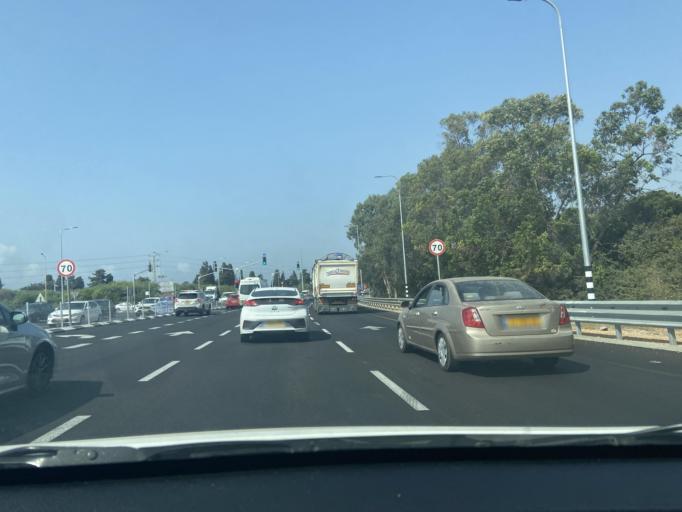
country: IL
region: Northern District
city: `Akko
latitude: 32.9503
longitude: 35.0915
